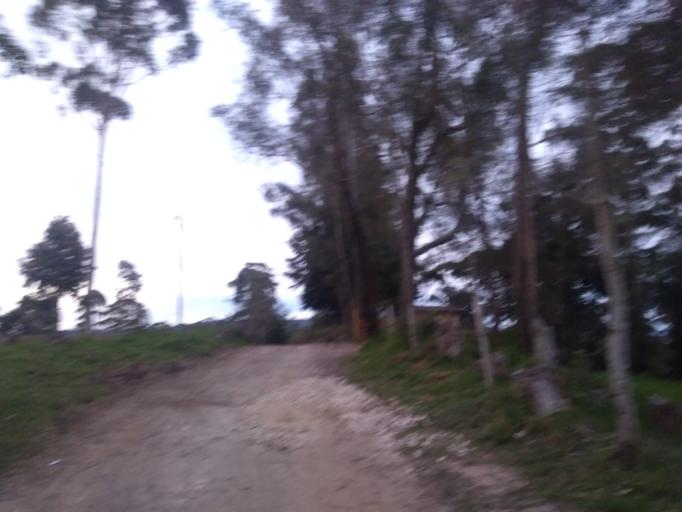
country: CO
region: Antioquia
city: Bello
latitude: 6.3560
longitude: -75.6039
